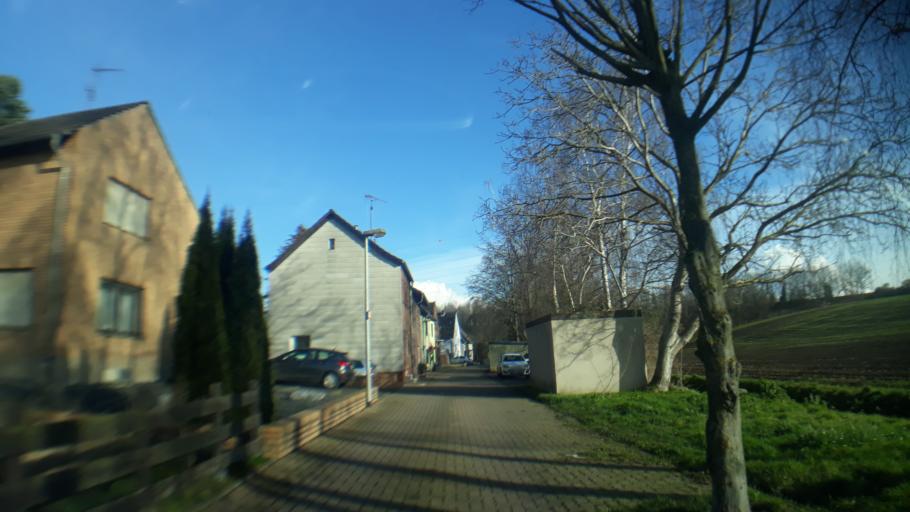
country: DE
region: North Rhine-Westphalia
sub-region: Regierungsbezirk Koln
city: Bedburg
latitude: 50.9889
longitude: 6.5500
